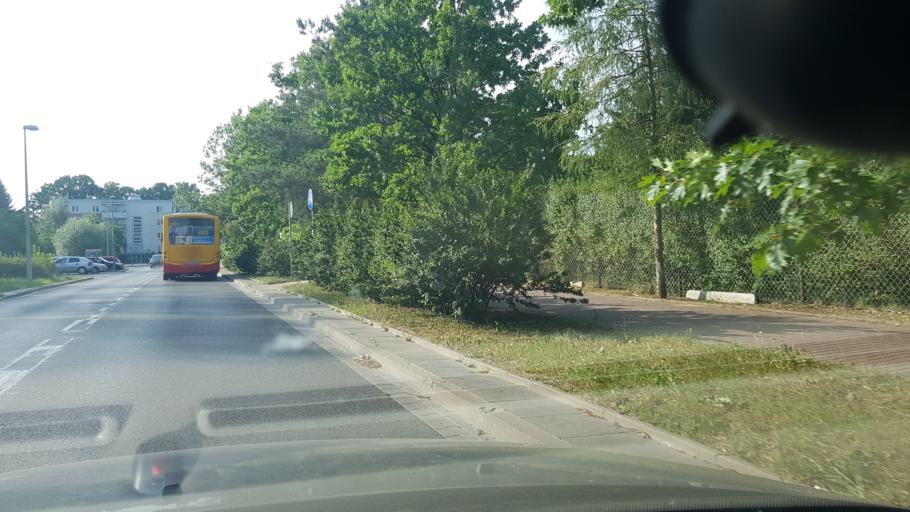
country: PL
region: Masovian Voivodeship
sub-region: Warszawa
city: Bialoleka
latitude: 52.3256
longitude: 20.9585
